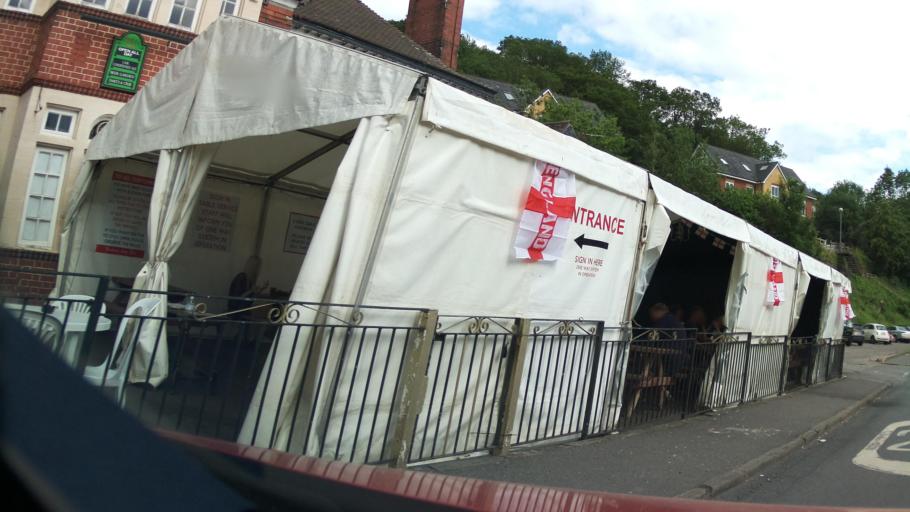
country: GB
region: England
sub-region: South Gloucestershire
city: Kingswood
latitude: 51.4521
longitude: -2.5356
